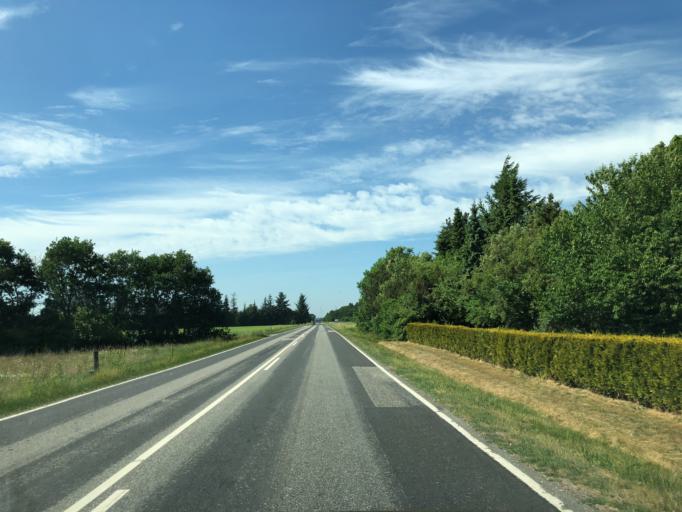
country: DK
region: South Denmark
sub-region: Vejle Kommune
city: Give
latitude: 55.8871
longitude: 9.2178
